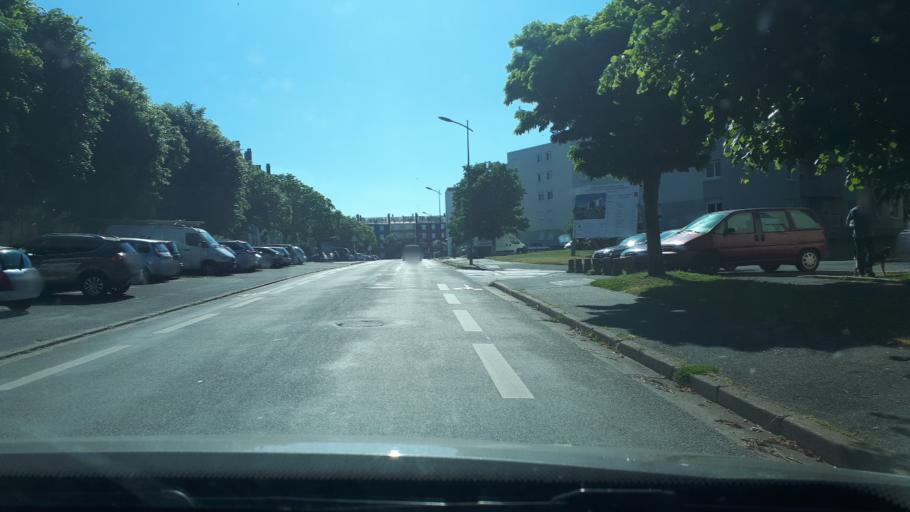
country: FR
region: Centre
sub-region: Departement du Loir-et-Cher
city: Vendome
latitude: 47.8067
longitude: 1.0688
